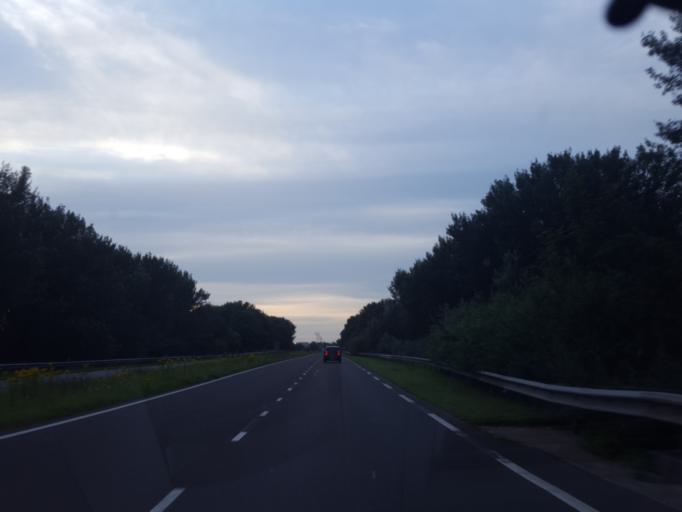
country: NL
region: Friesland
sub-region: Gemeente Leeuwarden
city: Camminghaburen
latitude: 53.2013
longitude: 5.8370
